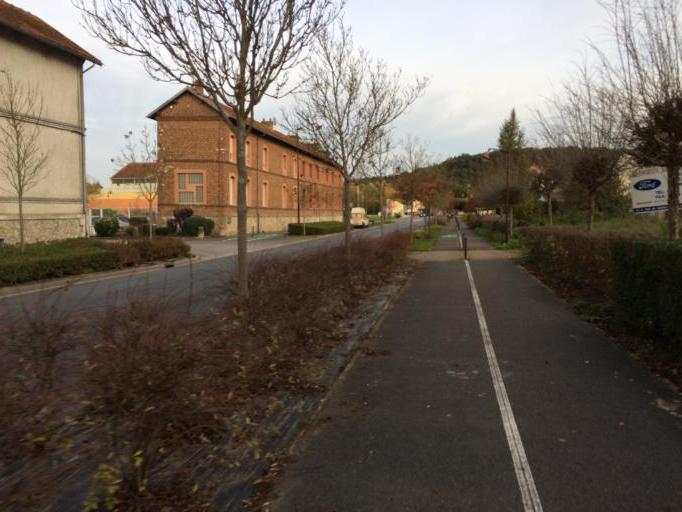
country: FR
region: Ile-de-France
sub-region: Departement de l'Essonne
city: Maisse
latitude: 48.3930
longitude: 2.3884
